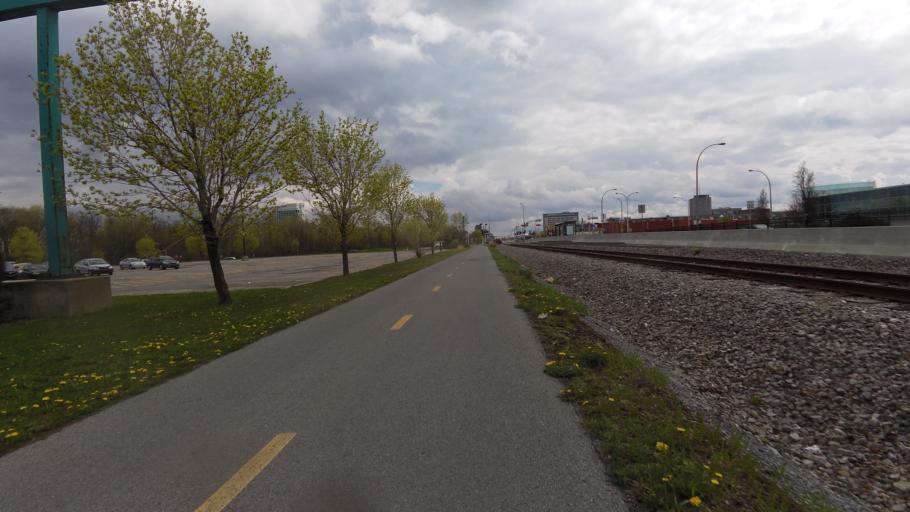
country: CA
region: Quebec
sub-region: Outaouais
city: Gatineau
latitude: 45.4532
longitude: -75.7294
